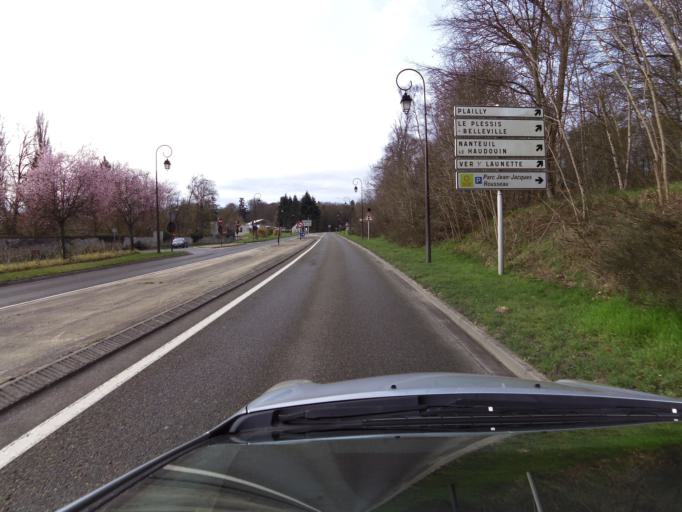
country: FR
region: Picardie
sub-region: Departement de l'Oise
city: Ver-sur-Launette
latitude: 49.1291
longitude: 2.6900
